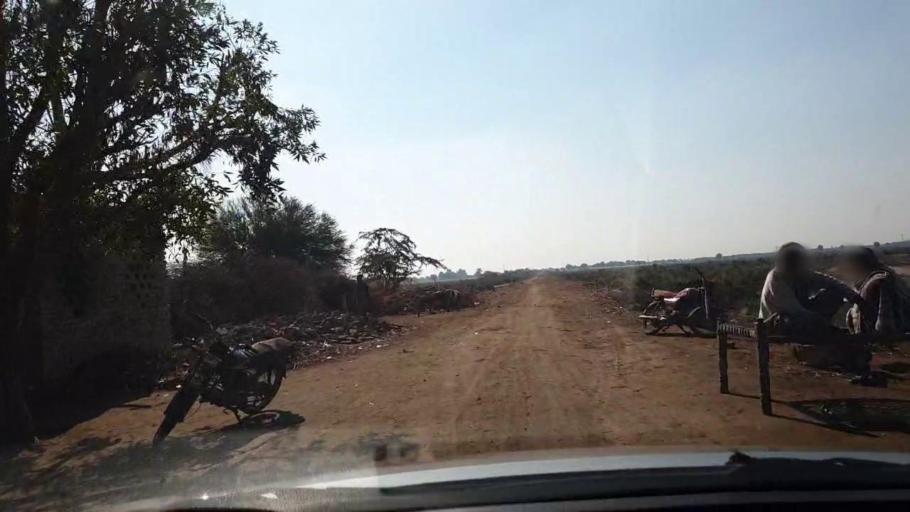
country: PK
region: Sindh
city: Jhol
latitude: 25.8754
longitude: 68.8952
